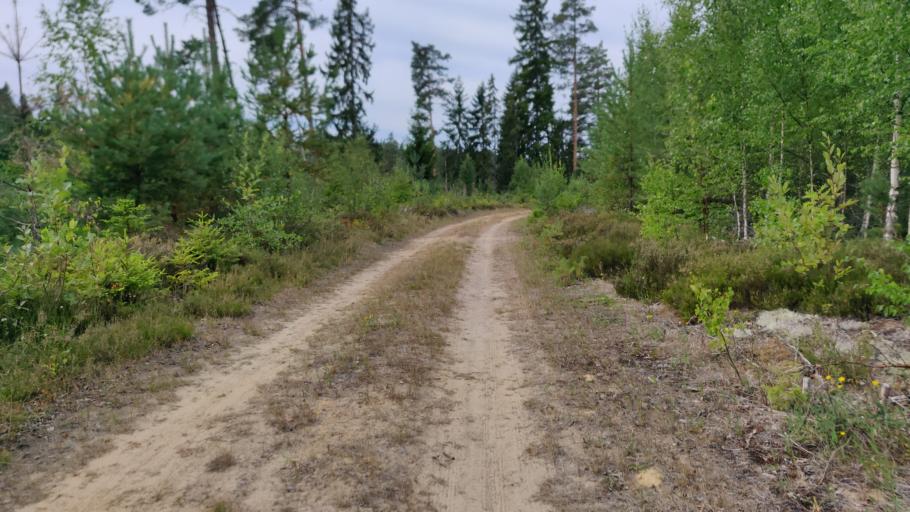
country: SE
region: Vaermland
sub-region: Hagfors Kommun
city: Hagfors
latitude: 60.0183
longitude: 13.5439
